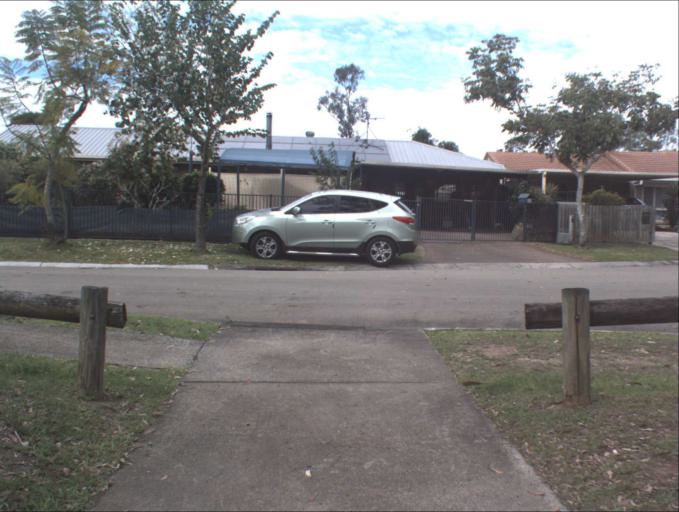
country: AU
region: Queensland
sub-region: Logan
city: Waterford West
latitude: -27.6878
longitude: 153.1271
